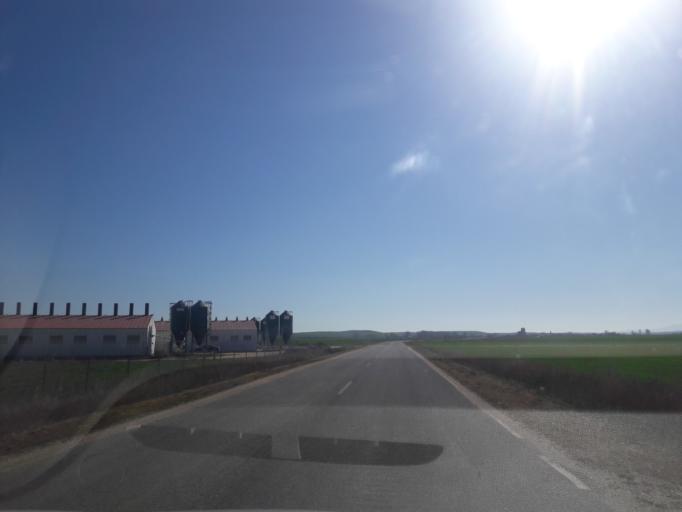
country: ES
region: Castille and Leon
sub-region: Provincia de Salamanca
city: Salmoral
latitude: 40.8091
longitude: -5.2416
